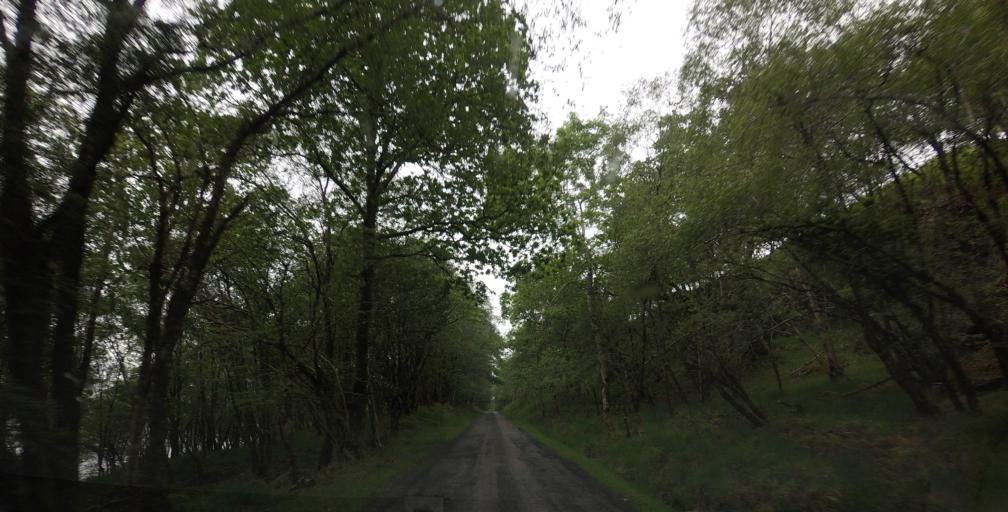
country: GB
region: Scotland
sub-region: Highland
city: Fort William
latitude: 56.8101
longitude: -5.1463
